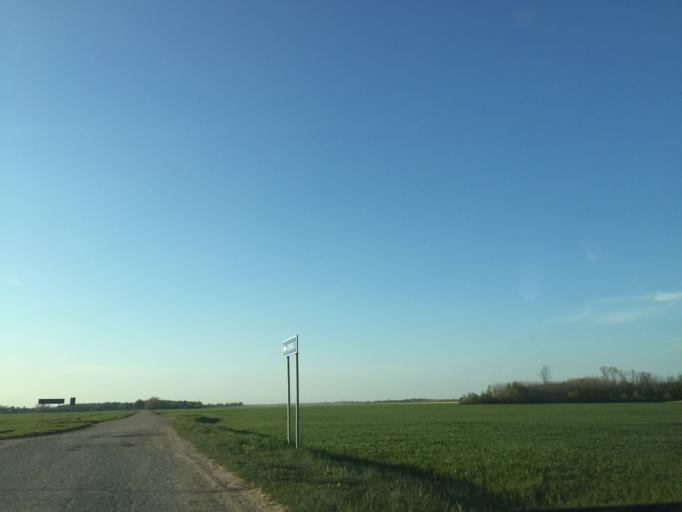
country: LV
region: Bauskas Rajons
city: Bauska
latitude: 56.2836
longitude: 24.2649
